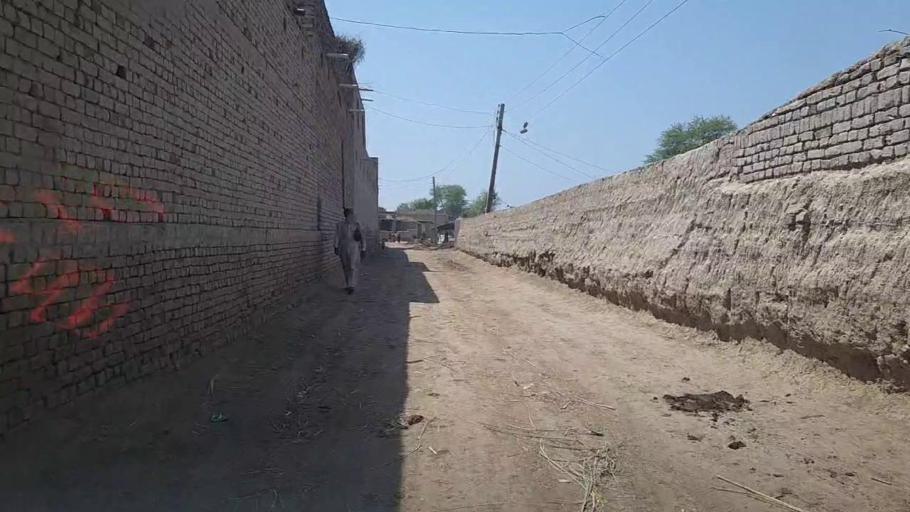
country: PK
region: Sindh
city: Ubauro
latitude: 28.1971
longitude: 69.8018
